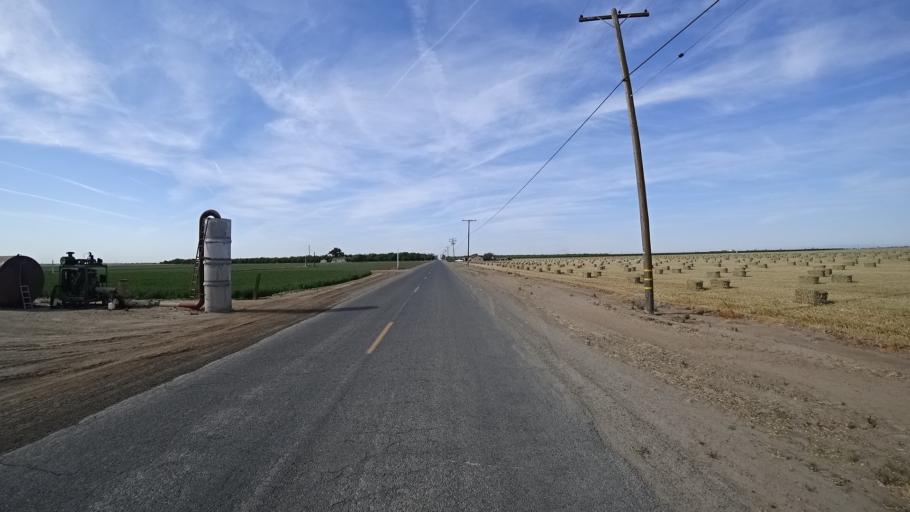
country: US
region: California
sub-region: Kings County
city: Hanford
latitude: 36.3646
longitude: -119.5471
